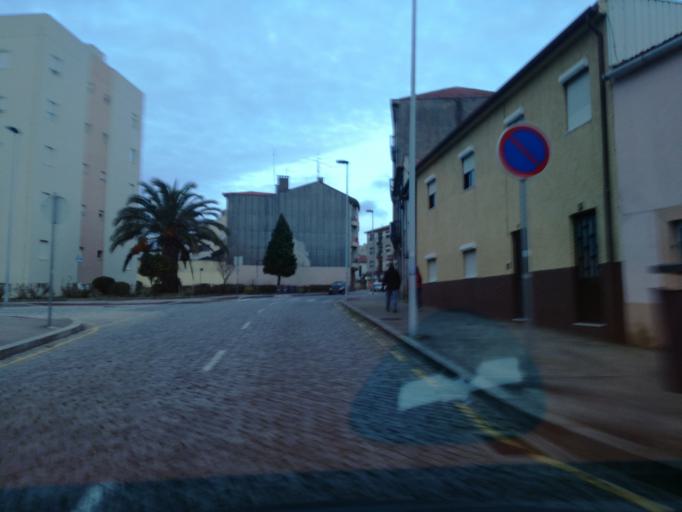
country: PT
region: Porto
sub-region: Vila Nova de Gaia
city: Canidelo
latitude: 41.1506
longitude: -8.6508
